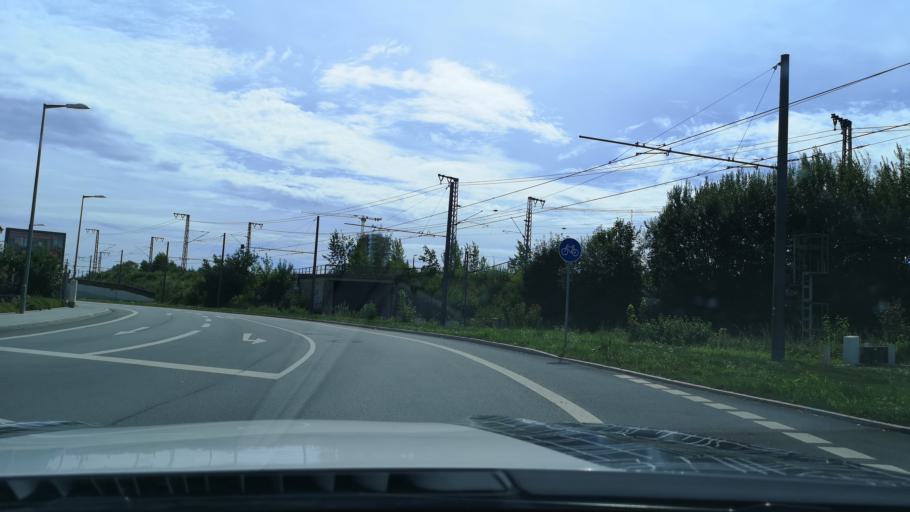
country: DE
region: Bavaria
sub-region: Upper Bavaria
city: Bogenhausen
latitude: 48.1359
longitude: 11.6245
